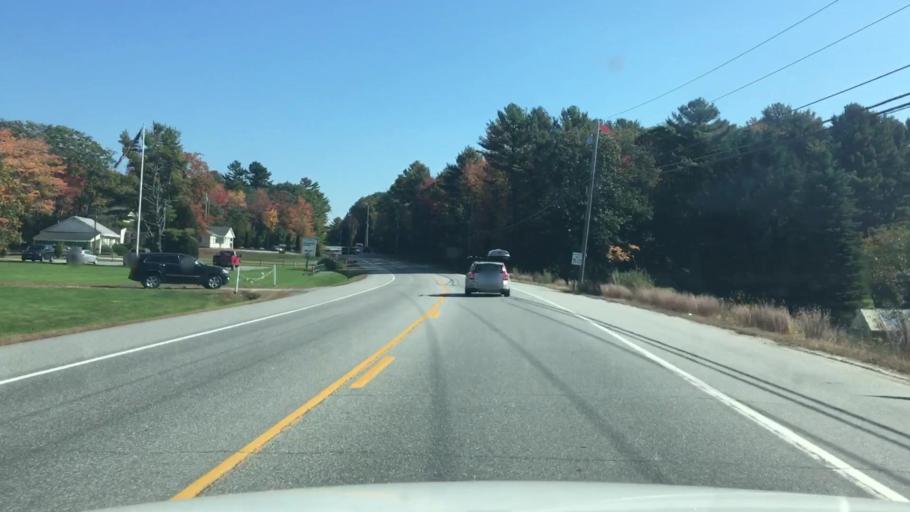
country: US
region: Maine
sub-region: Sagadahoc County
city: Topsham
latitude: 43.9622
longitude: -70.0142
